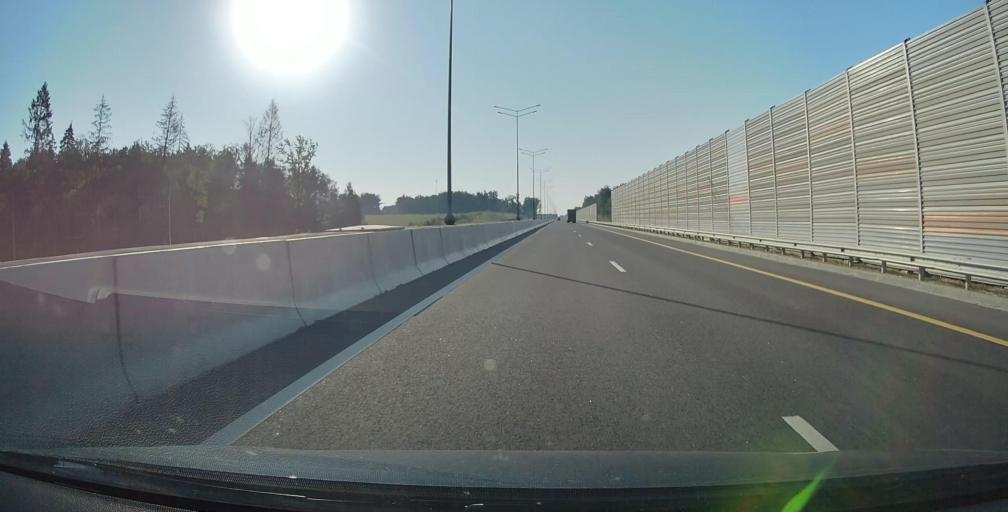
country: RU
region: Moskovskaya
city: Yel'digino
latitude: 56.1512
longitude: 37.7795
